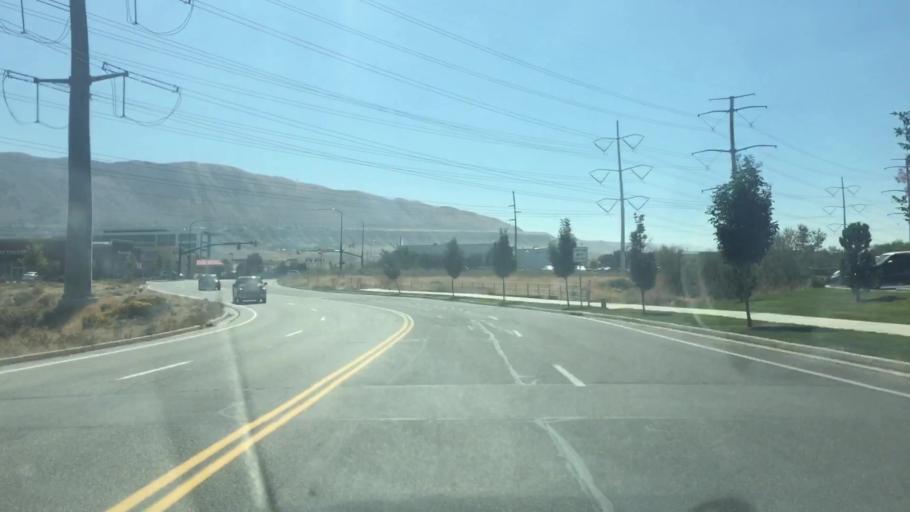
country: US
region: Utah
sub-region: Salt Lake County
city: Draper
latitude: 40.5078
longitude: -111.8974
